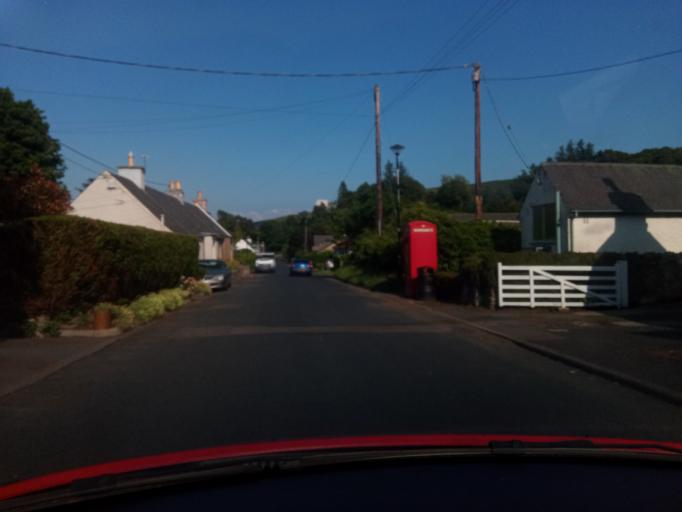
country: GB
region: Scotland
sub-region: The Scottish Borders
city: Selkirk
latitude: 55.5085
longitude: -2.9710
